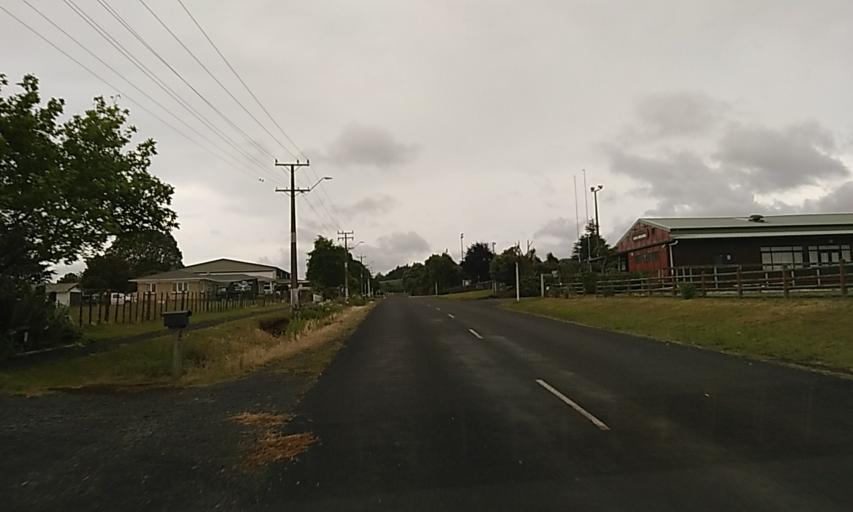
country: NZ
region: Auckland
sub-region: Auckland
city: Pukekohe East
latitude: -37.3294
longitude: 174.9148
